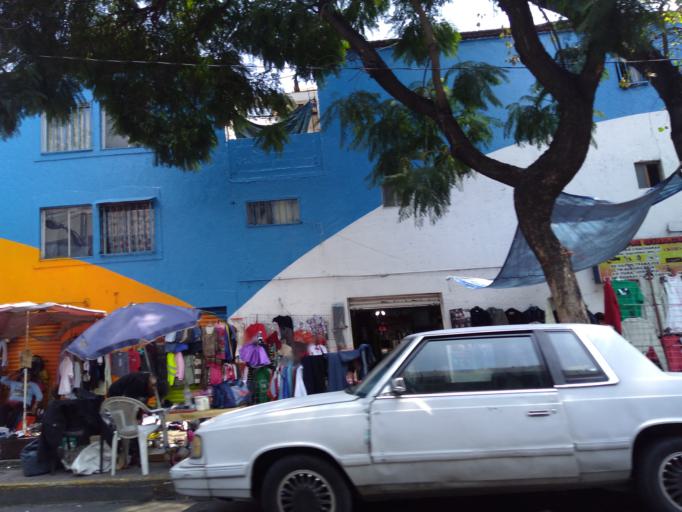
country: MX
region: Mexico City
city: Mexico City
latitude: 19.4406
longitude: -99.1179
